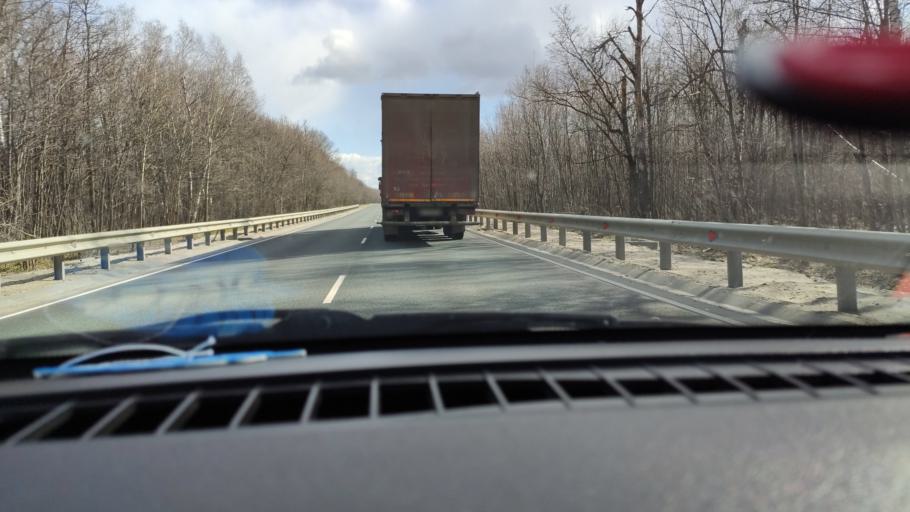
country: RU
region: Saratov
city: Khvalynsk
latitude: 52.4662
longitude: 48.0172
